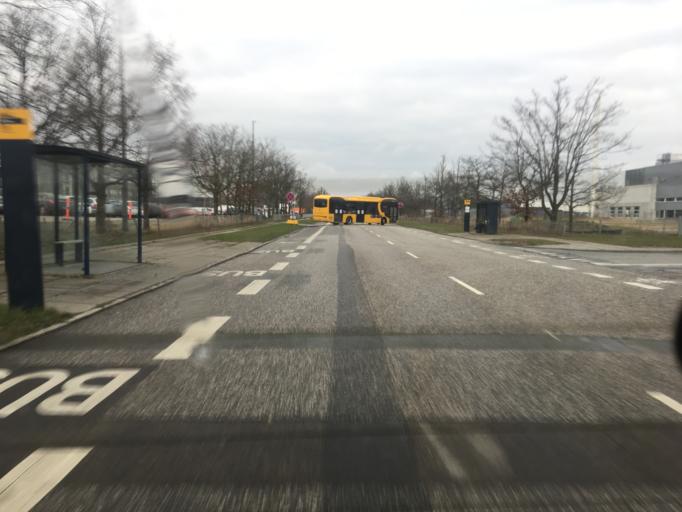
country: DK
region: Capital Region
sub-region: Hvidovre Kommune
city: Hvidovre
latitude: 55.6091
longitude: 12.4897
